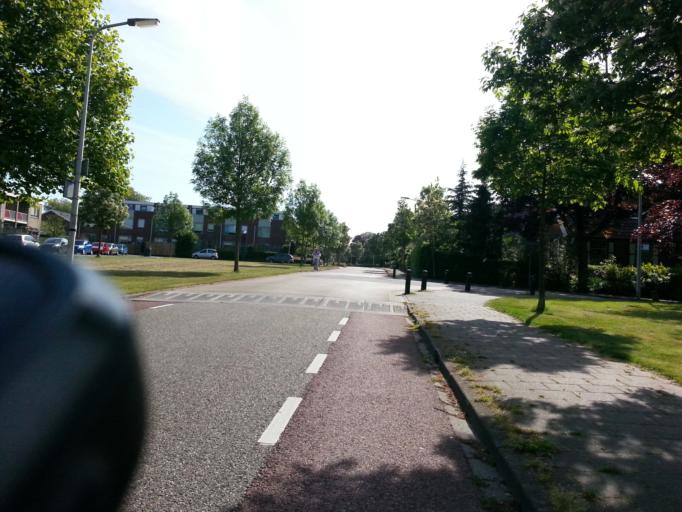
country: NL
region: Gelderland
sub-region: Berkelland
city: Eibergen
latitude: 52.0984
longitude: 6.6350
